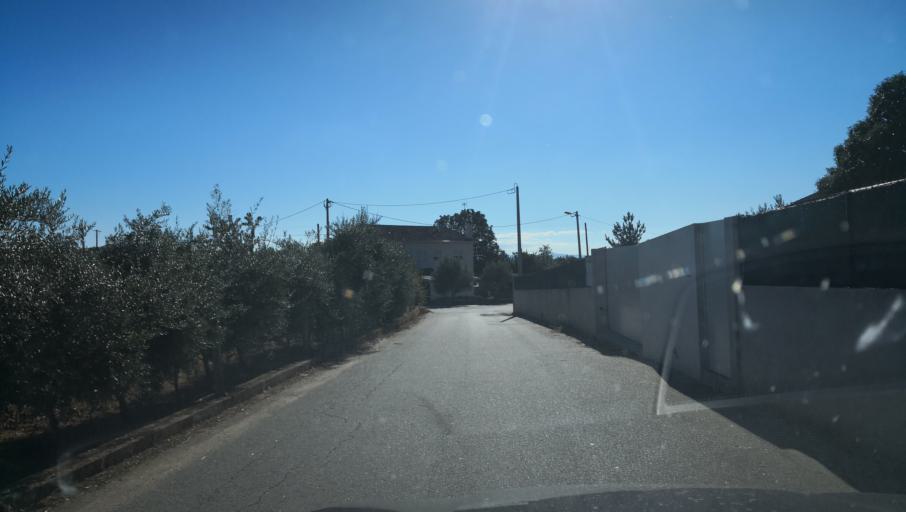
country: PT
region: Vila Real
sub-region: Vila Real
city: Vila Real
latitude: 41.2715
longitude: -7.7025
